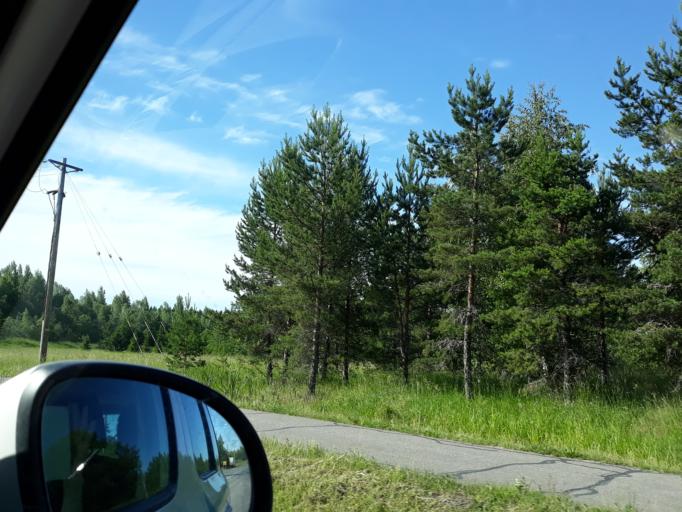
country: FI
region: Uusimaa
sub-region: Helsinki
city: Jaervenpaeae
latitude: 60.5483
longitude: 24.9795
